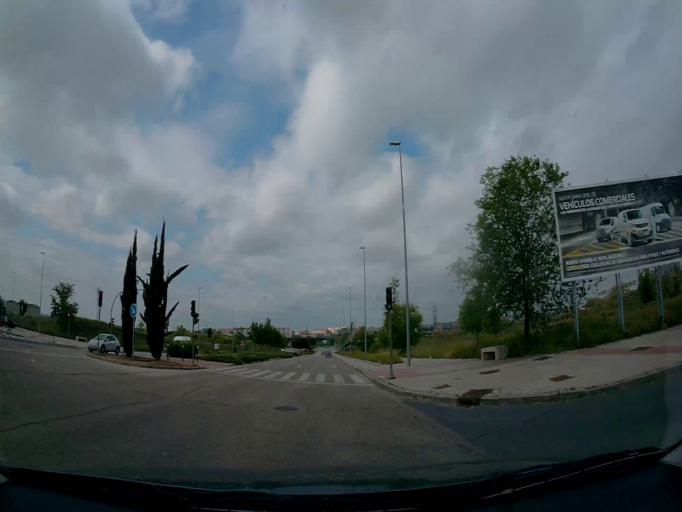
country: ES
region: Madrid
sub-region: Provincia de Madrid
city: Alcorcon
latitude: 40.3283
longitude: -3.8375
